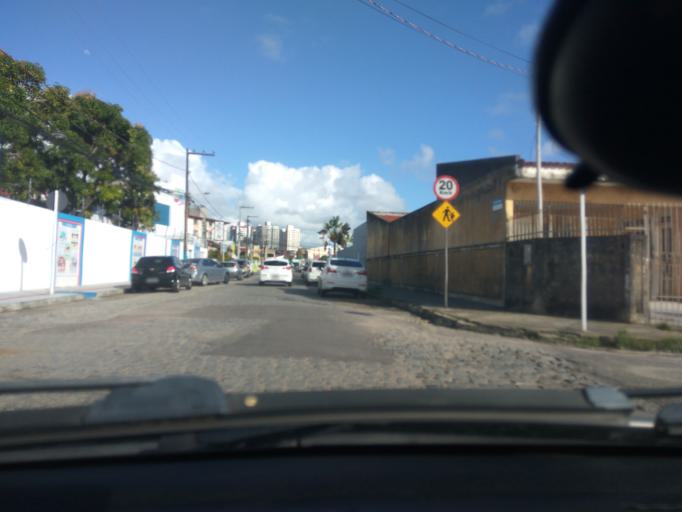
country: BR
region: Sergipe
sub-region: Aracaju
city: Aracaju
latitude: -10.9453
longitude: -37.0633
